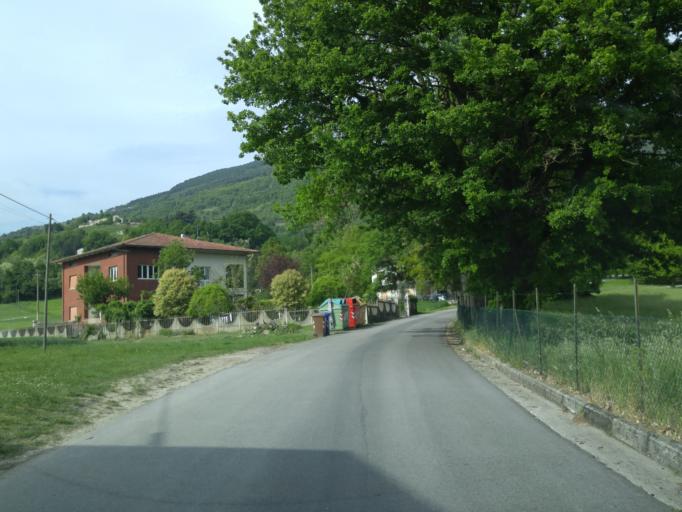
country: IT
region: The Marches
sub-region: Provincia di Pesaro e Urbino
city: Acqualagna
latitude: 43.6390
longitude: 12.6907
